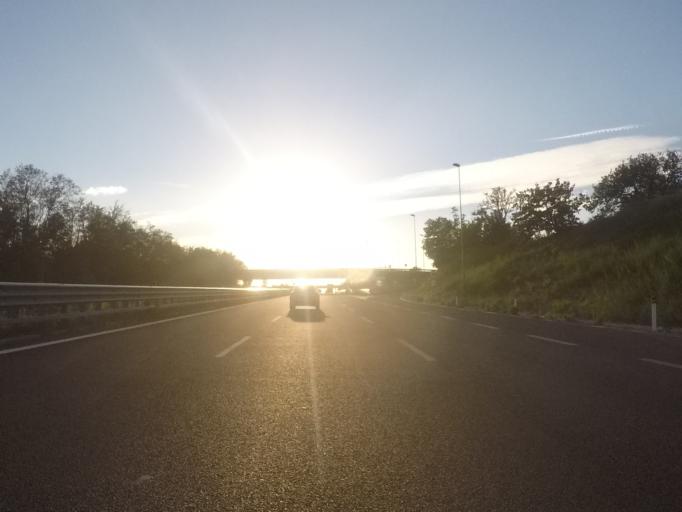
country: IT
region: Campania
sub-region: Provincia di Salerno
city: Quadrivio
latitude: 40.6073
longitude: 15.1216
